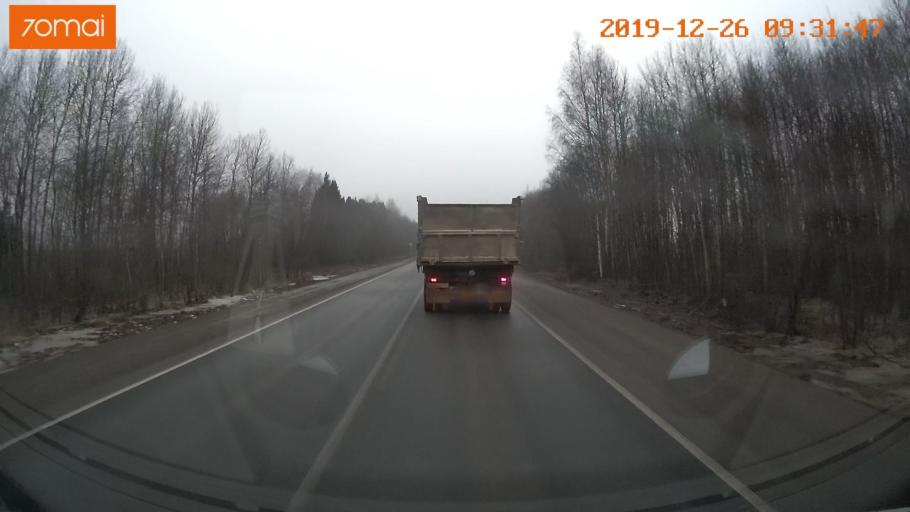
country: RU
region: Vologda
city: Gryazovets
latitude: 59.0721
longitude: 40.1241
